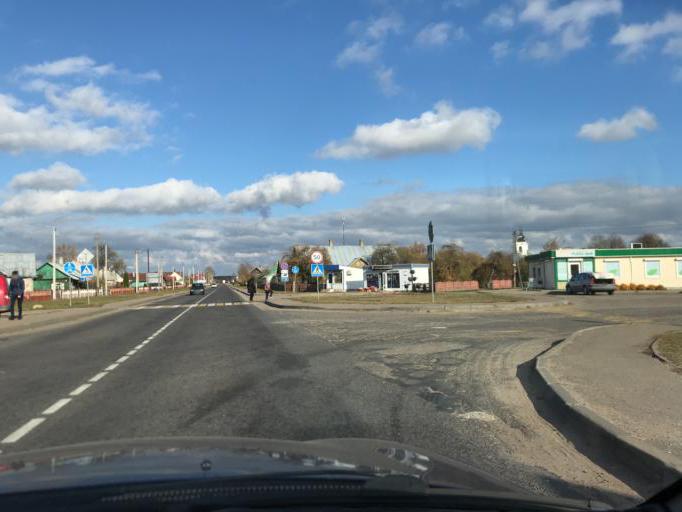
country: LT
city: Salcininkai
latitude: 54.2503
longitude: 25.3562
